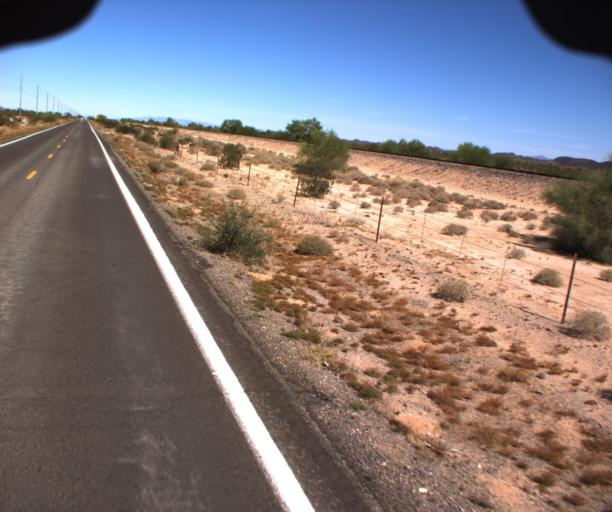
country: US
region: Arizona
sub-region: La Paz County
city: Salome
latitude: 33.8699
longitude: -113.9305
